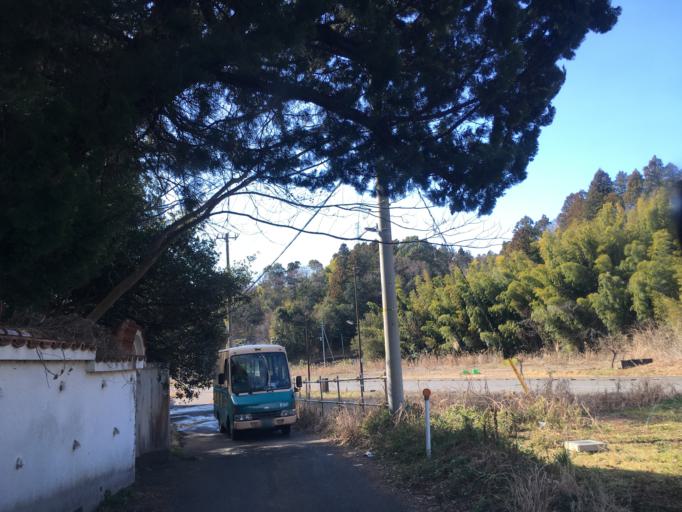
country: JP
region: Tokyo
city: Hino
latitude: 35.6049
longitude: 139.4084
